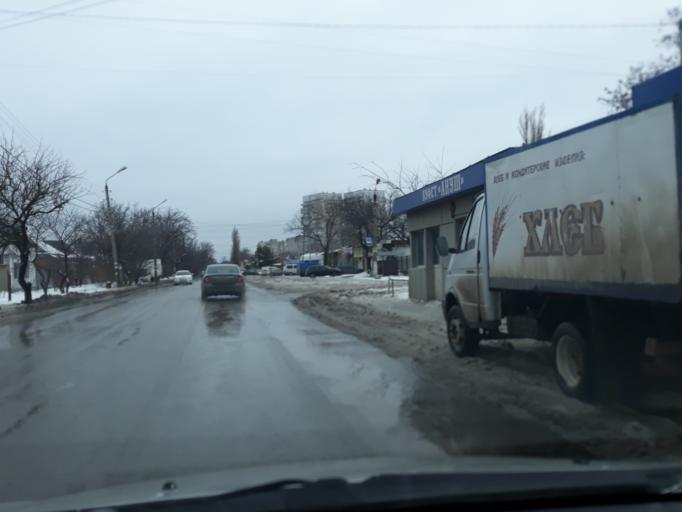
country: RU
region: Rostov
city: Taganrog
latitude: 47.2327
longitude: 38.8765
